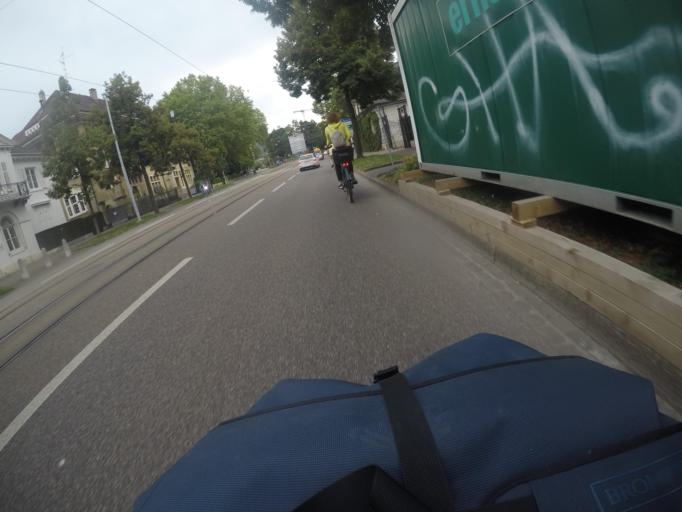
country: CH
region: Basel-City
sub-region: Basel-Stadt
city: Basel
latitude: 47.5489
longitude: 7.5973
